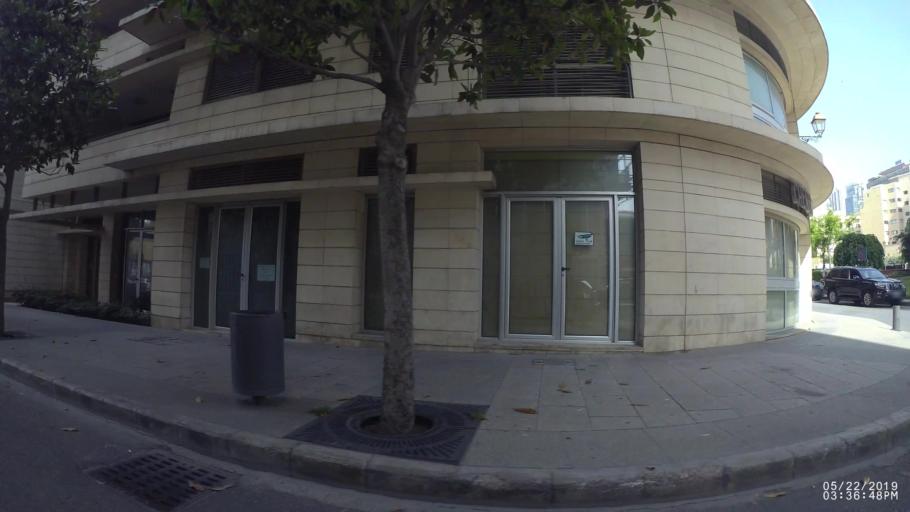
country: LB
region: Beyrouth
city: Beirut
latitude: 33.8939
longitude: 35.5070
